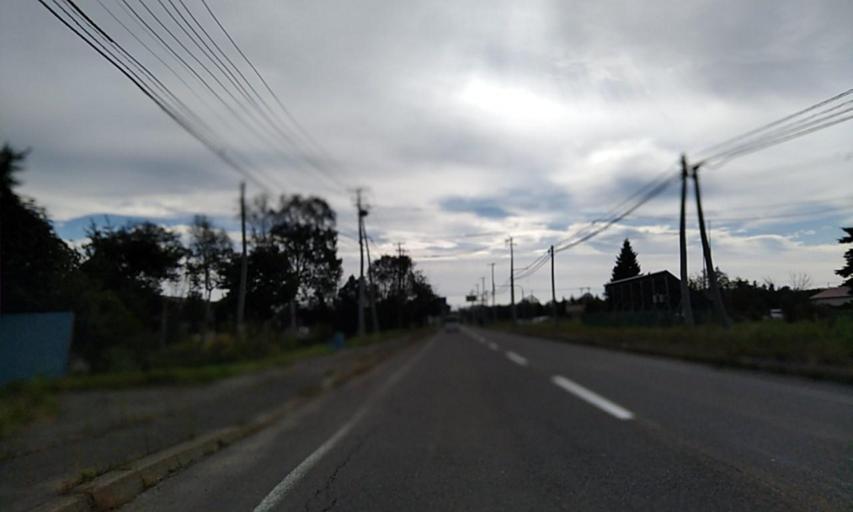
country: JP
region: Hokkaido
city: Obihiro
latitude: 42.8447
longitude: 143.1765
